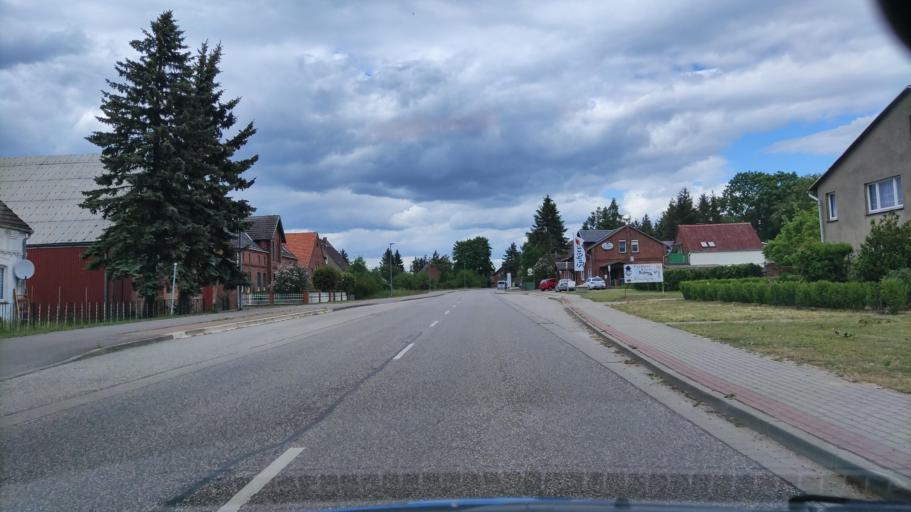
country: DE
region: Mecklenburg-Vorpommern
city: Spornitz
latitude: 53.3848
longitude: 11.6679
